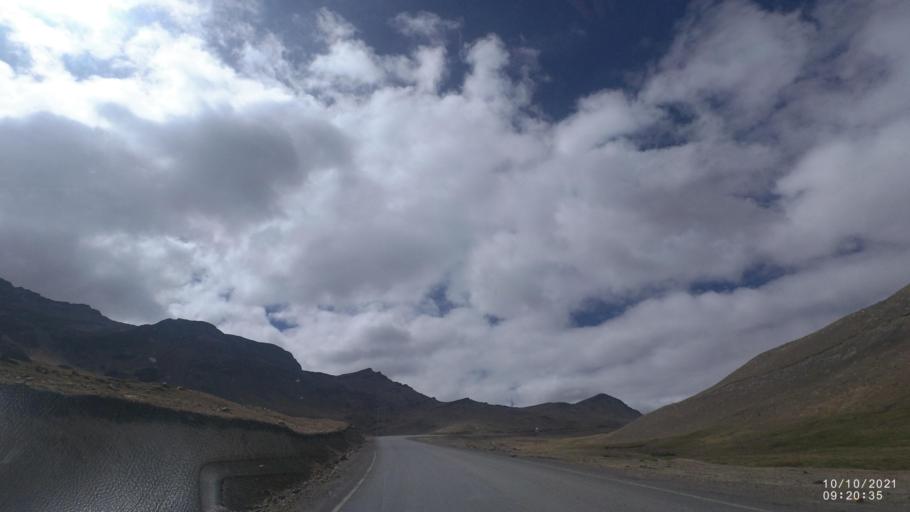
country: BO
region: La Paz
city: Quime
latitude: -17.0607
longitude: -67.2996
